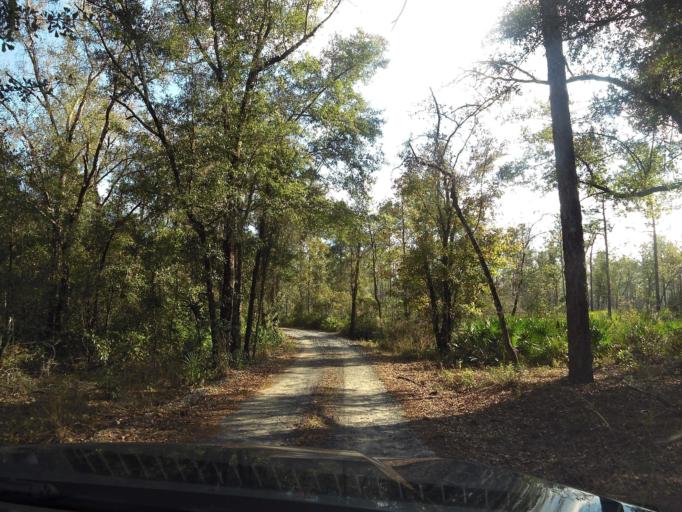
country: US
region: Florida
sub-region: Clay County
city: Middleburg
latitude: 30.1374
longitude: -81.9561
